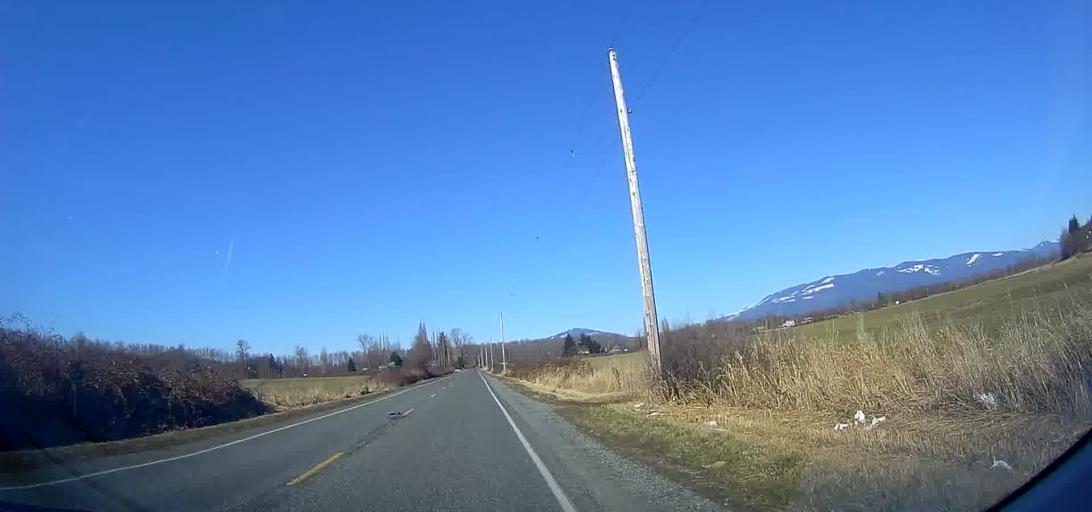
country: US
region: Washington
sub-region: Skagit County
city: Burlington
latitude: 48.4587
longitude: -122.3028
